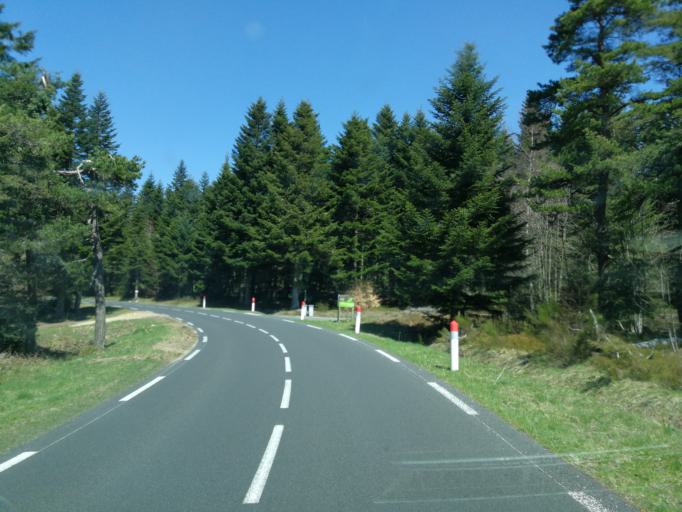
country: FR
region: Rhone-Alpes
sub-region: Departement de l'Ardeche
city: Saint-Agreve
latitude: 45.0976
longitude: 4.4019
